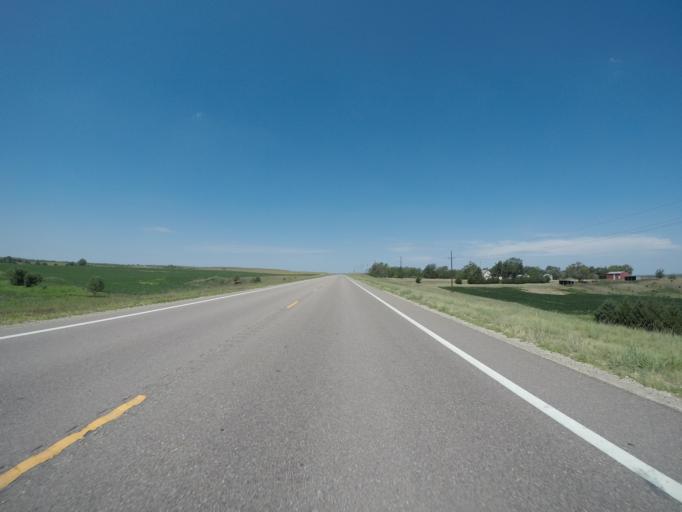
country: US
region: Kansas
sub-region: Osborne County
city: Osborne
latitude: 39.5099
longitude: -98.6611
